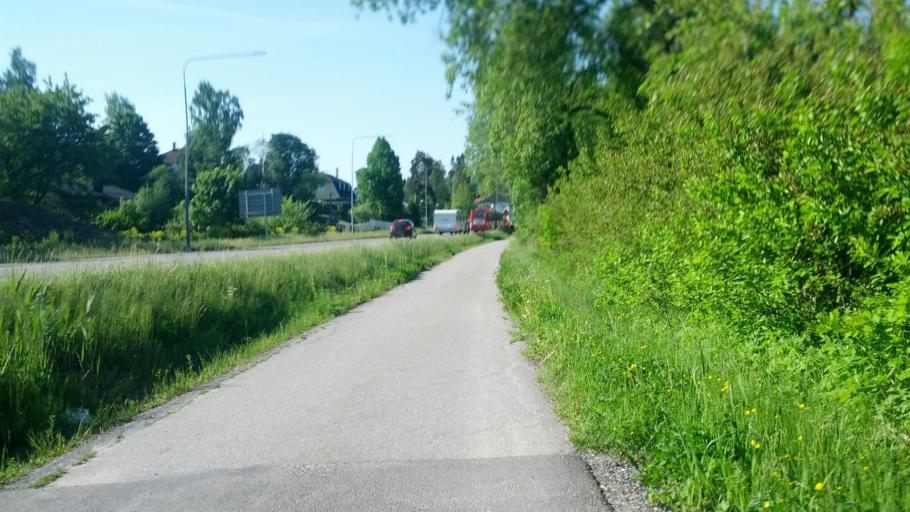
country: SE
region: Stockholm
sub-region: Taby Kommun
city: Taby
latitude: 59.4540
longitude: 18.0362
